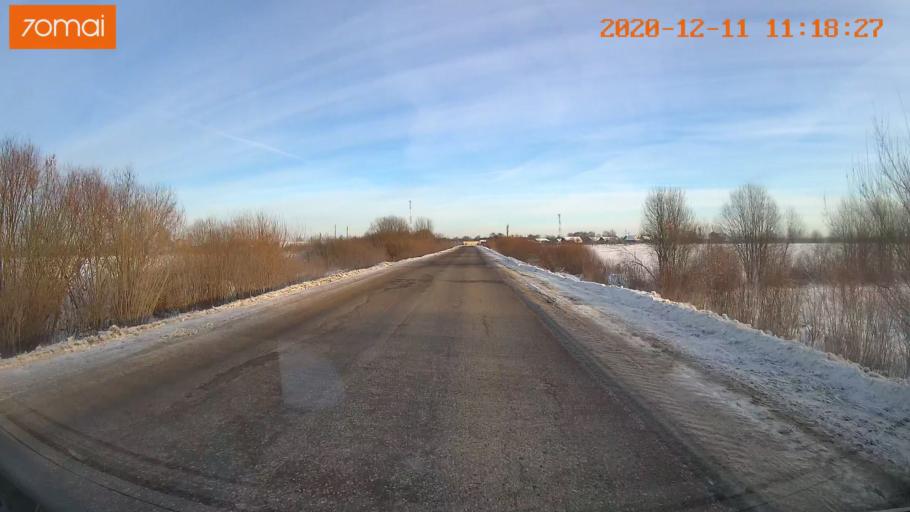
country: RU
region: Jaroslavl
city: Lyubim
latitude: 58.3196
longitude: 40.9984
